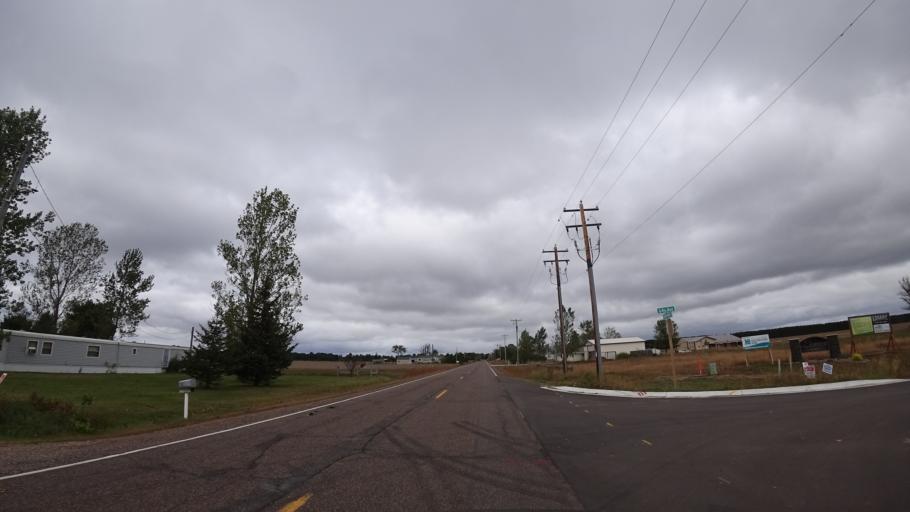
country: US
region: Wisconsin
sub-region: Chippewa County
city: Lake Wissota
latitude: 44.9360
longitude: -91.2679
